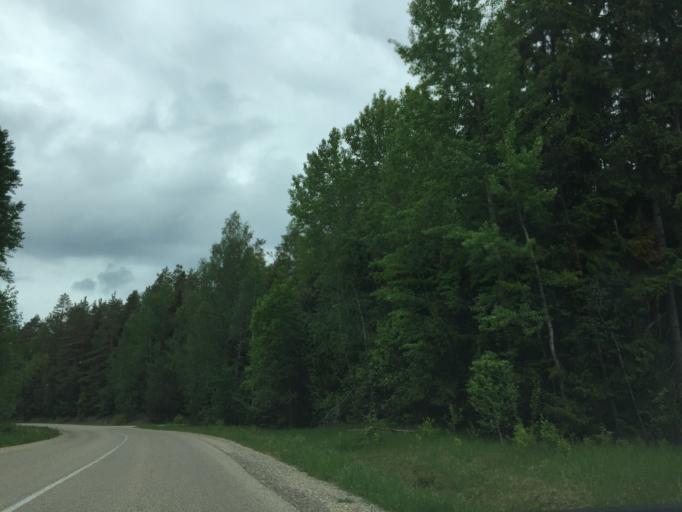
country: LV
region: Varkava
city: Vecvarkava
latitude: 56.0768
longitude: 26.6259
